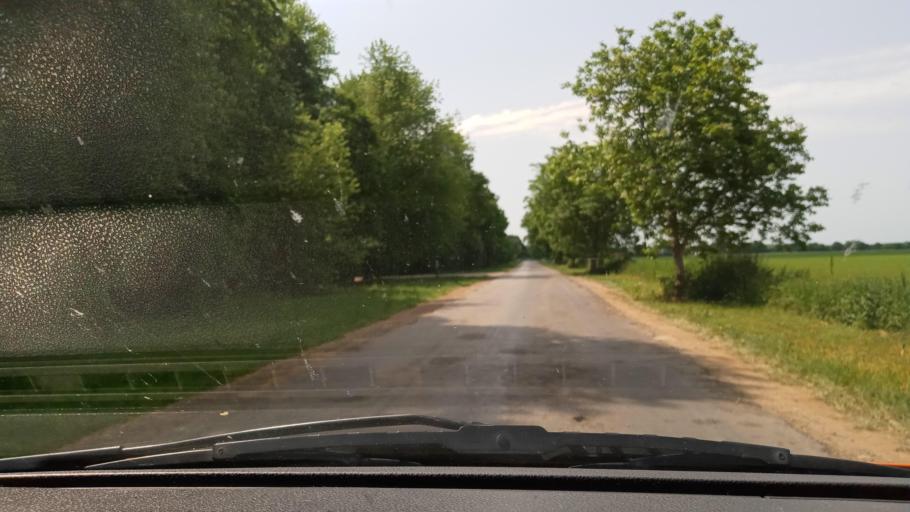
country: HU
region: Baranya
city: Szentlorinc
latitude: 46.0001
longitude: 18.0372
